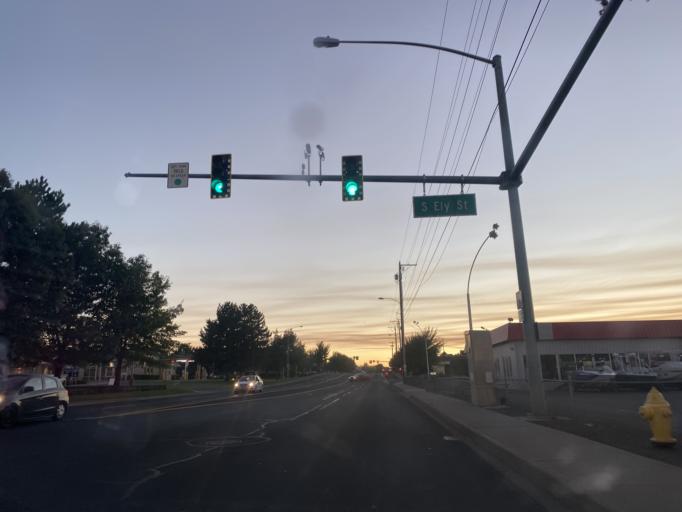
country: US
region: Washington
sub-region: Benton County
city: Kennewick
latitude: 46.1987
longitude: -119.1569
